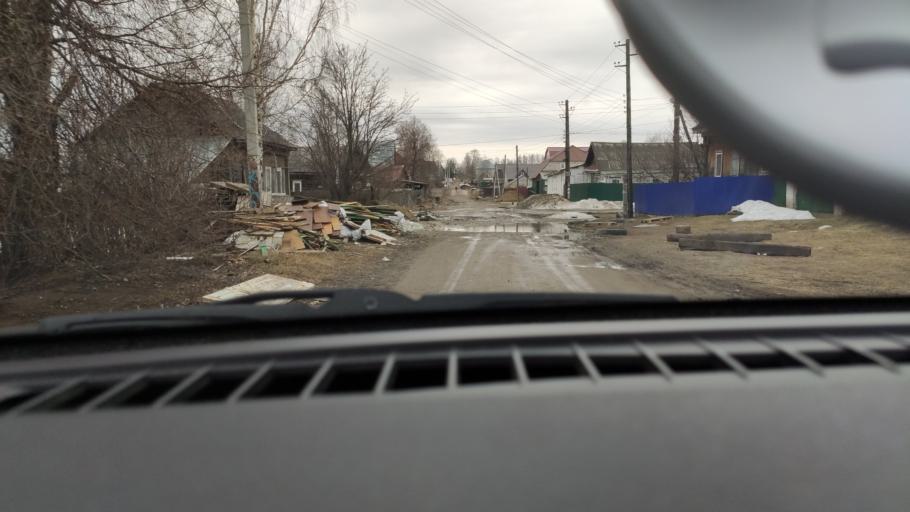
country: RU
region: Perm
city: Kondratovo
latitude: 58.0489
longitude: 56.0422
